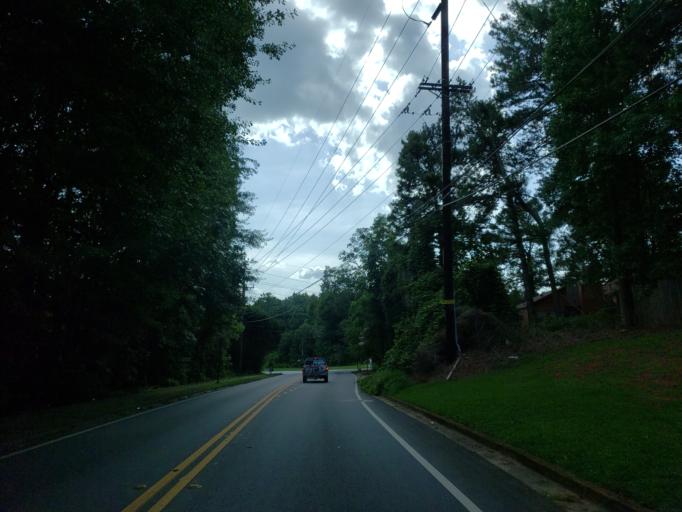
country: US
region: Georgia
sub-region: Cobb County
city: Powder Springs
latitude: 33.8768
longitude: -84.6577
